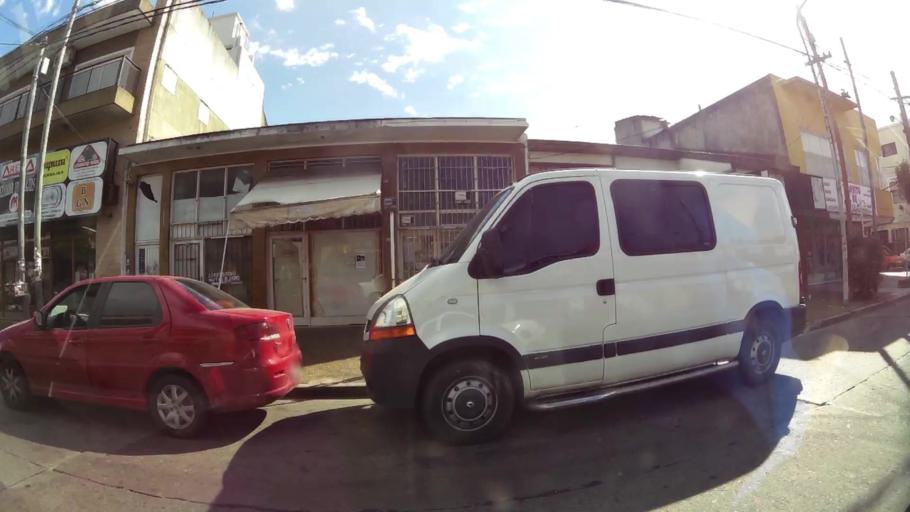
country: AR
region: Buenos Aires
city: San Justo
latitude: -34.6680
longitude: -58.5751
